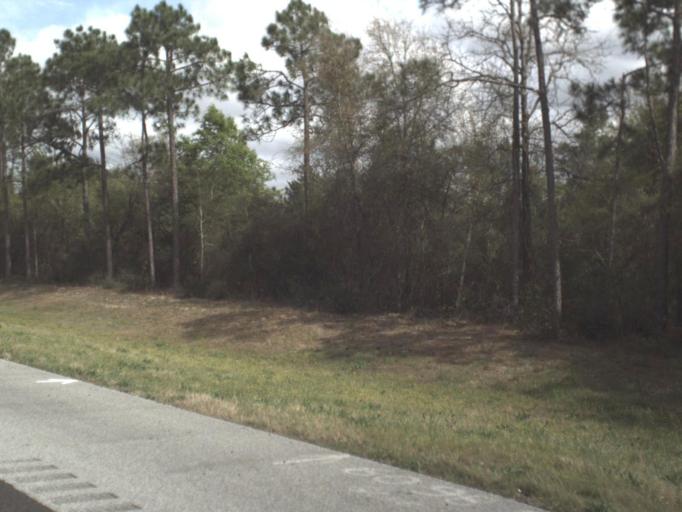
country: US
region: Florida
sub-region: Walton County
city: DeFuniak Springs
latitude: 30.7480
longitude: -86.2922
